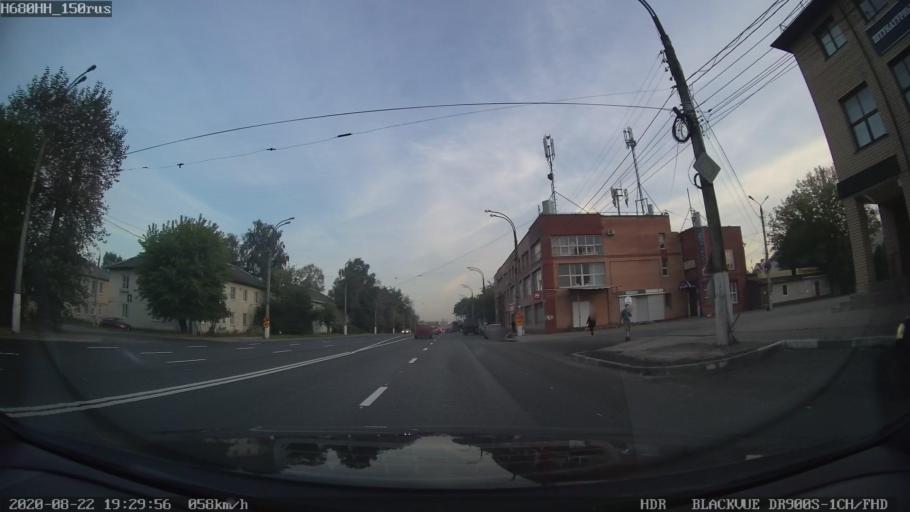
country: RU
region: Tverskaya
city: Tver
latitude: 56.8661
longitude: 35.9443
